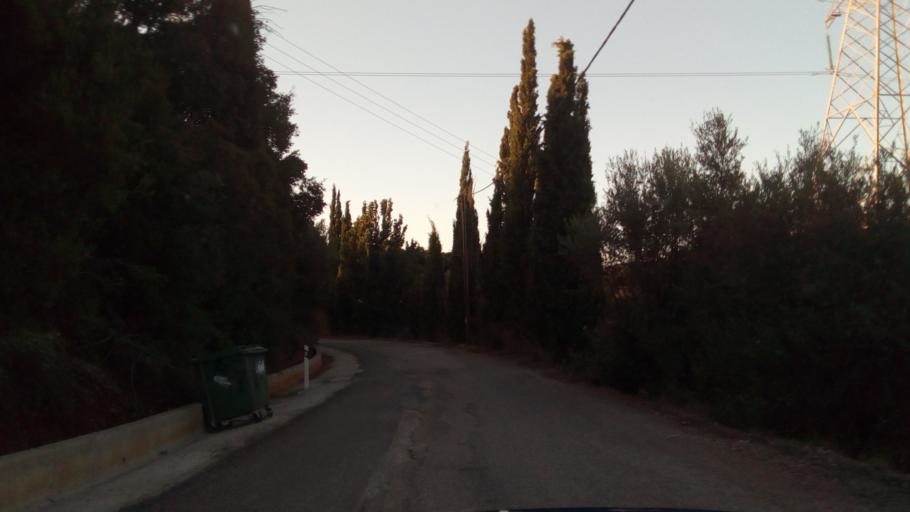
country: GR
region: West Greece
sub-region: Nomos Aitolias kai Akarnanias
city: Nafpaktos
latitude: 38.4051
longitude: 21.7963
